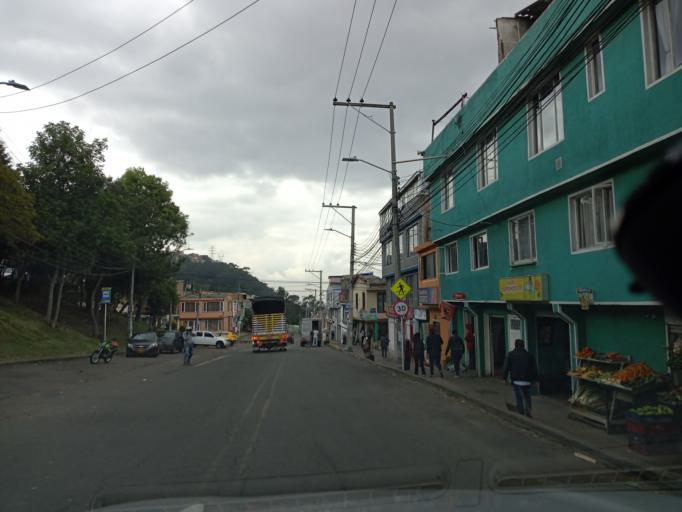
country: CO
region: Bogota D.C.
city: Bogota
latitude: 4.5671
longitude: -74.1047
